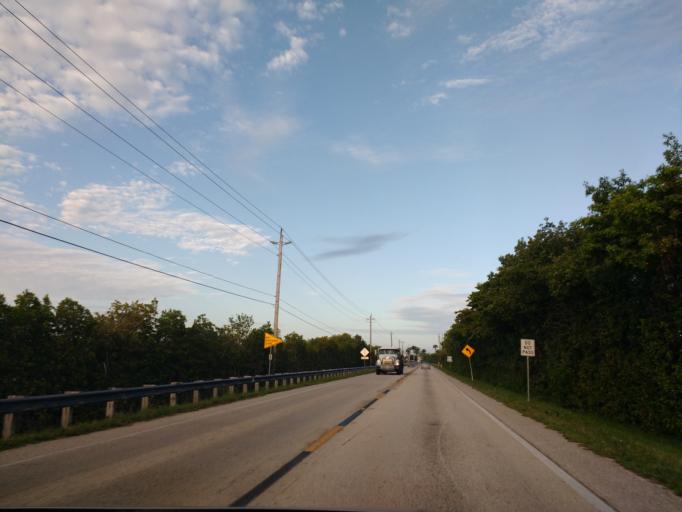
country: US
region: Florida
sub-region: Lee County
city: Pine Island Center
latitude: 26.6379
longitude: -82.0611
